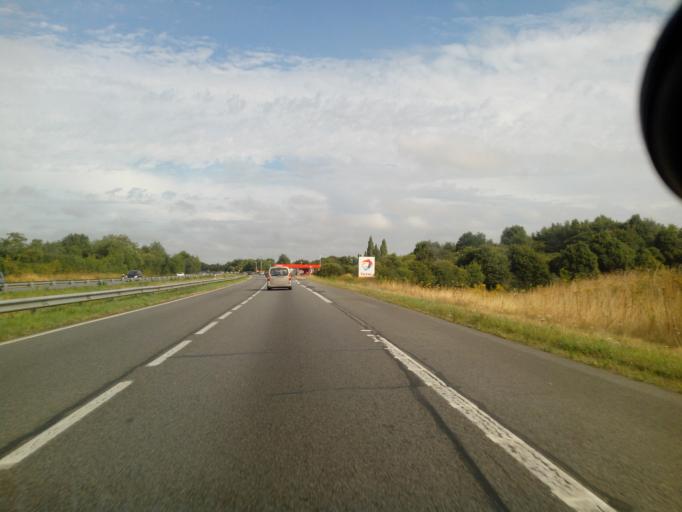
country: FR
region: Pays de la Loire
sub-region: Departement de la Loire-Atlantique
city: Le Temple-de-Bretagne
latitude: 47.3274
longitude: -1.7815
